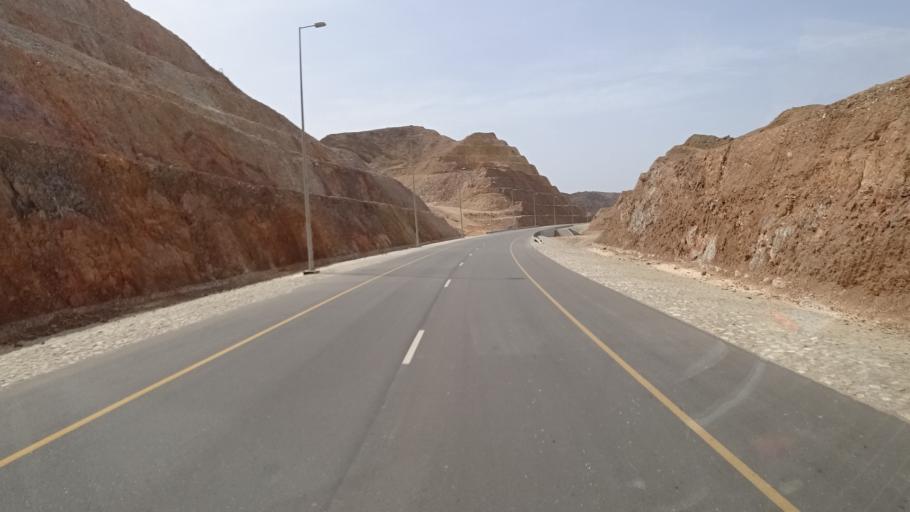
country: OM
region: Muhafazat Masqat
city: Muscat
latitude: 23.5095
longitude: 58.7232
